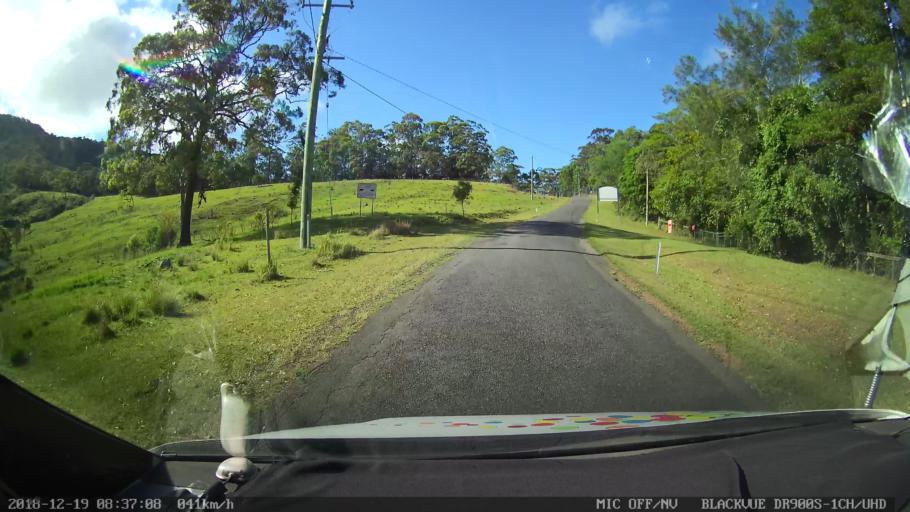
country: AU
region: New South Wales
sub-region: Kyogle
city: Kyogle
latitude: -28.3305
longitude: 152.9733
